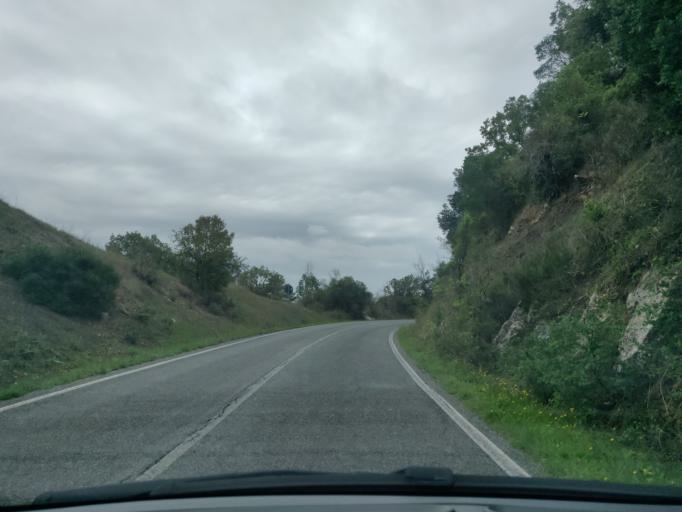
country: IT
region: Latium
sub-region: Citta metropolitana di Roma Capitale
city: Allumiere
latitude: 42.1377
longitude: 11.8715
